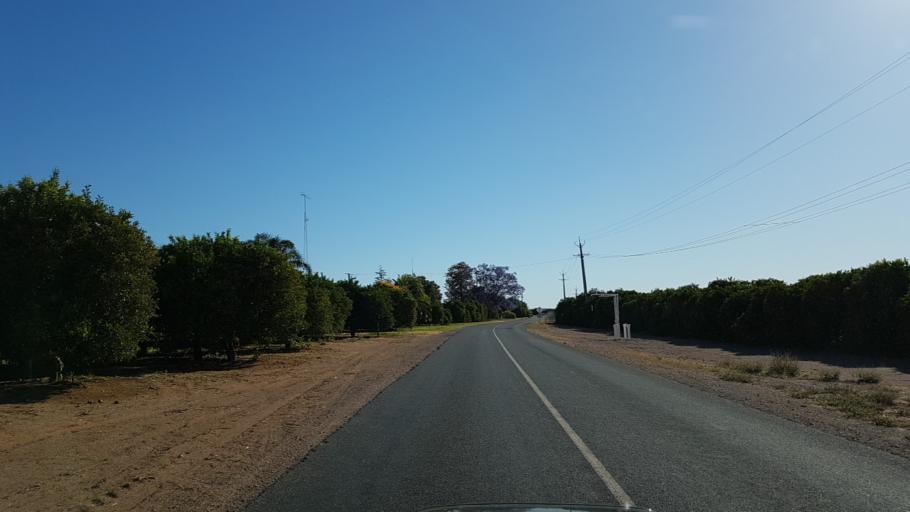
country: AU
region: South Australia
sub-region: Loxton Waikerie
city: Waikerie
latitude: -34.1749
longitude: 140.0298
